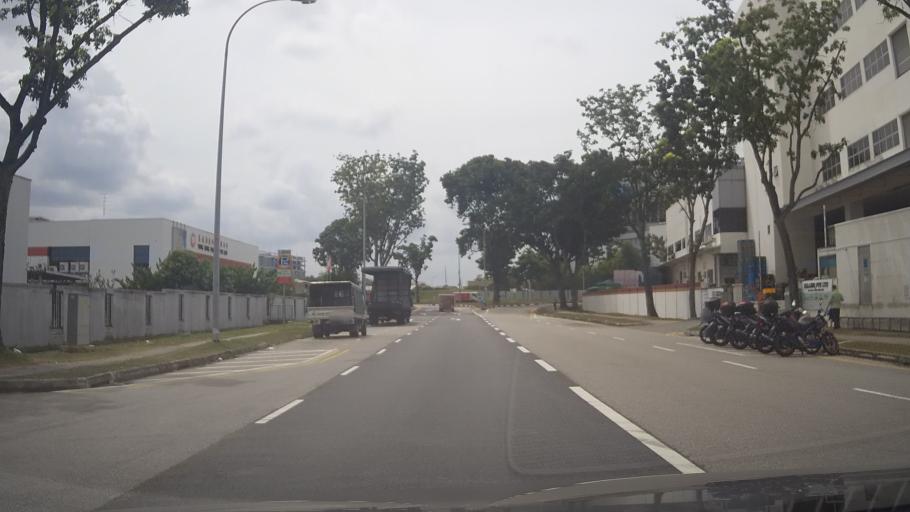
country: MY
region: Johor
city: Johor Bahru
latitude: 1.4550
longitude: 103.8024
